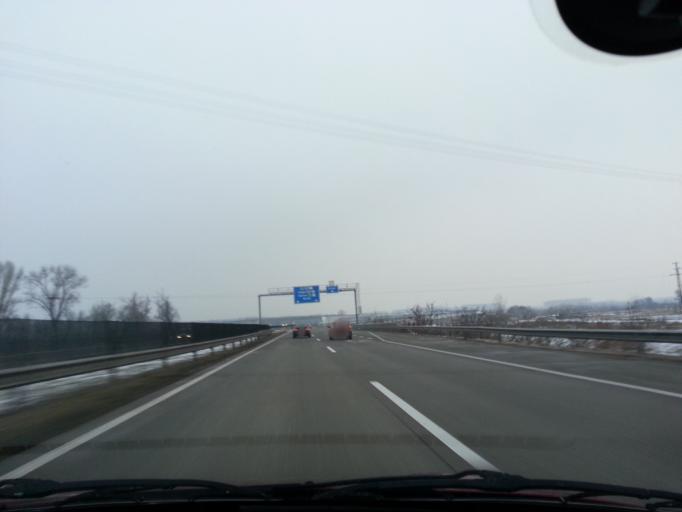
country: HU
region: Pest
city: Ecser
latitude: 47.4355
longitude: 19.3291
